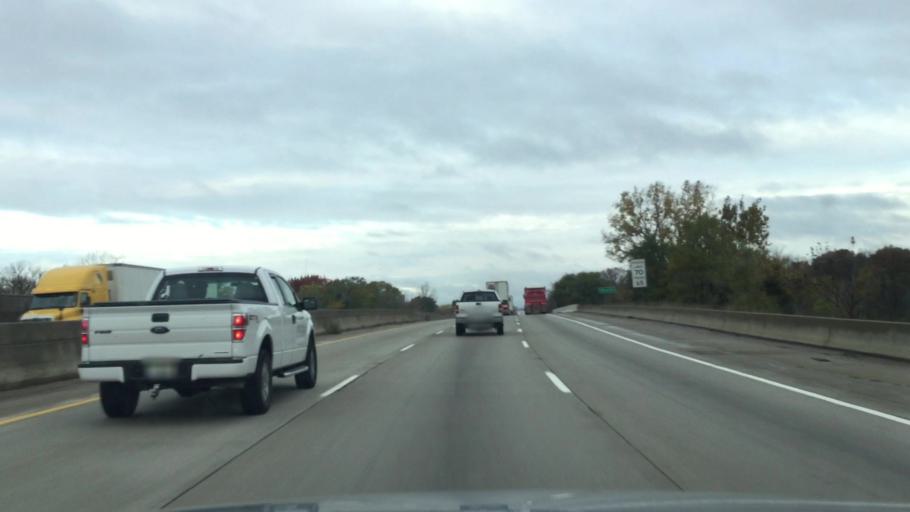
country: US
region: Michigan
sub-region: Washtenaw County
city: Ypsilanti
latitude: 42.2193
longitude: -83.5612
